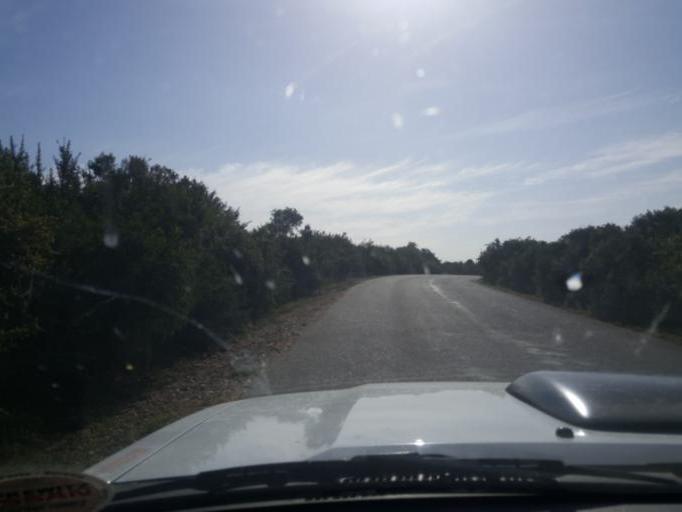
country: ZA
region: Eastern Cape
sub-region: Cacadu District Municipality
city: Kirkwood
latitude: -33.4418
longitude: 25.7555
